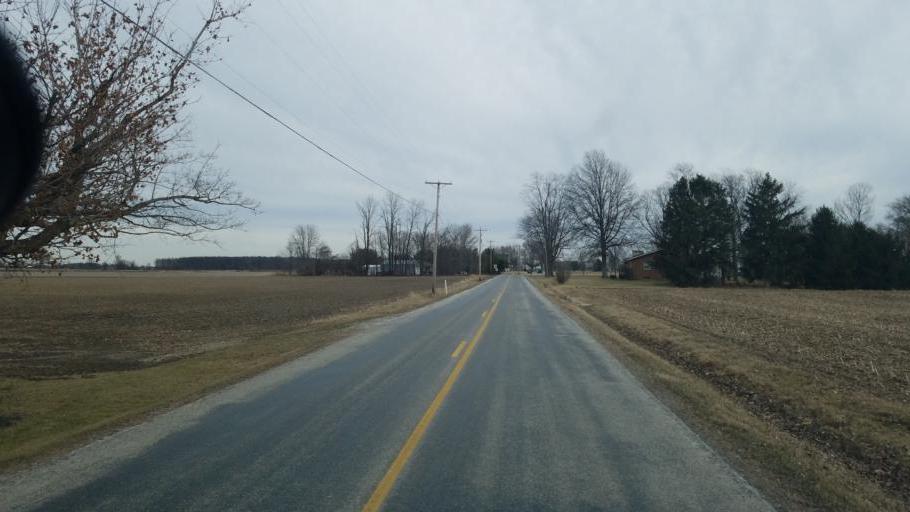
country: US
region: Ohio
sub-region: Delaware County
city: Ashley
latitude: 40.4564
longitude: -83.0214
